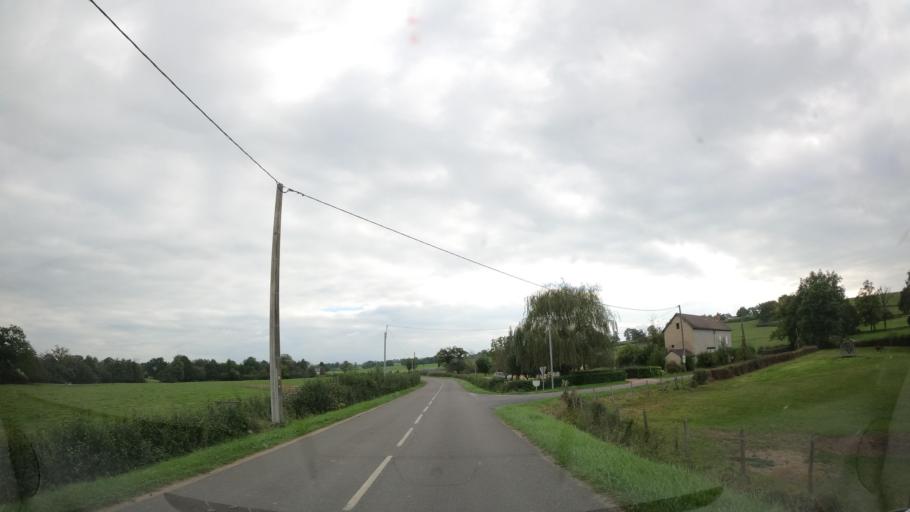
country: FR
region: Auvergne
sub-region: Departement de l'Allier
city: Lapalisse
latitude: 46.3231
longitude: 3.6309
